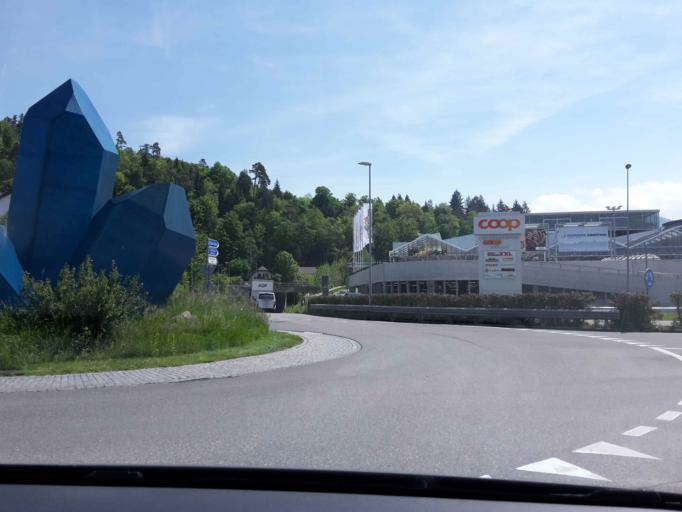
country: CH
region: Bern
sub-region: Thun District
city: Heimberg
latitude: 46.7808
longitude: 7.6078
